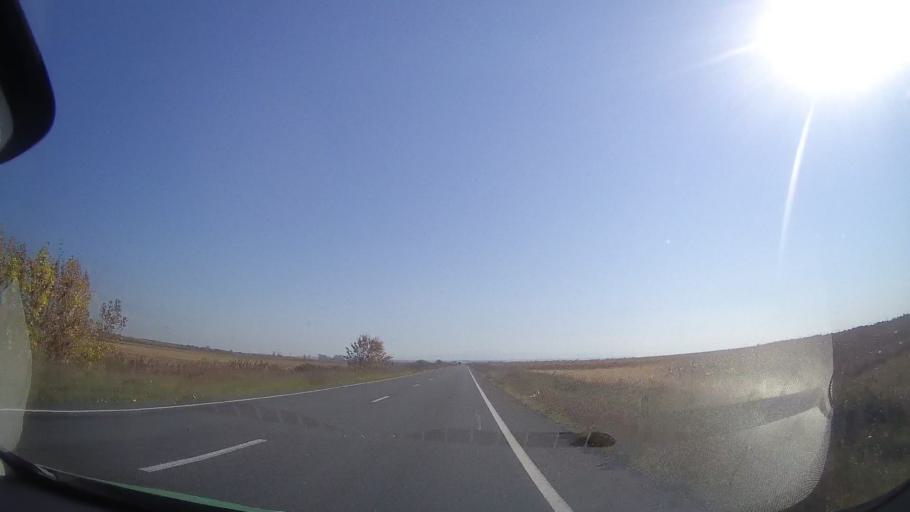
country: RO
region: Timis
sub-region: Comuna Belint
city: Belint
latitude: 45.7456
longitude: 21.7998
